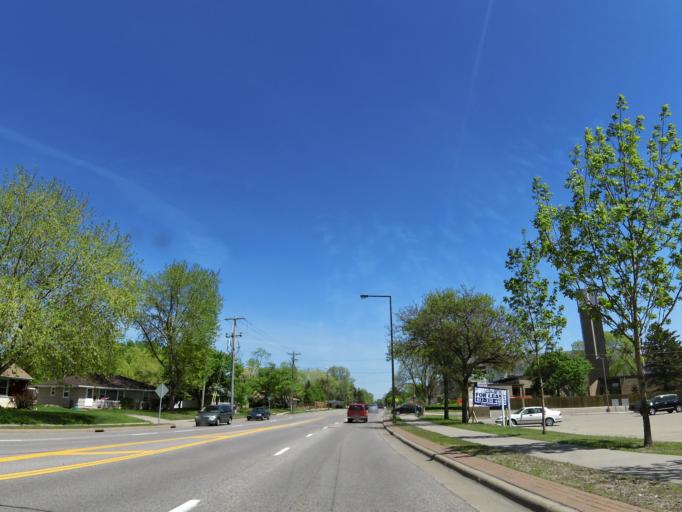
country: US
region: Minnesota
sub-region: Scott County
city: Savage
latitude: 44.8108
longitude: -93.3278
